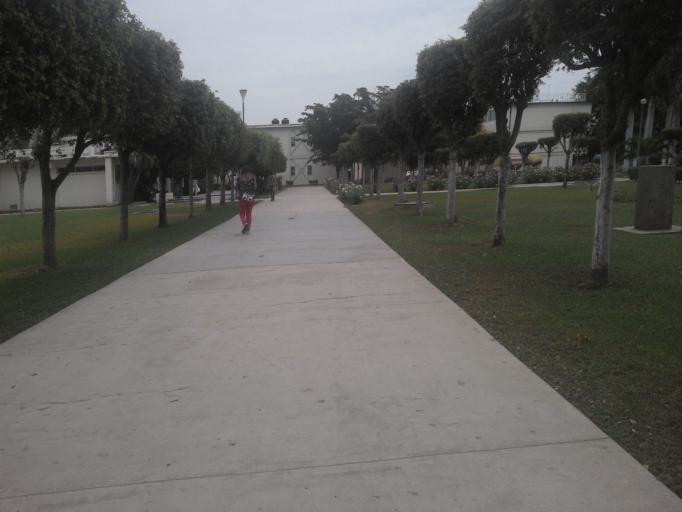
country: MX
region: Sinaloa
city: Culiacan
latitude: 24.8276
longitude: -107.3812
